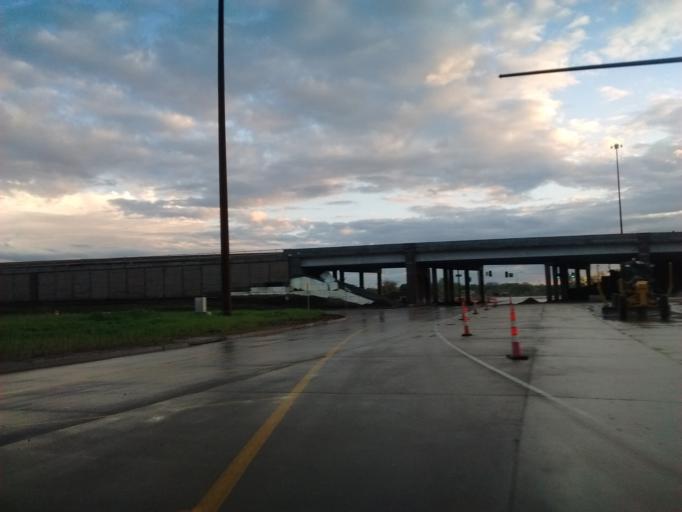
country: US
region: Iowa
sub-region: Woodbury County
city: Sioux City
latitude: 42.4875
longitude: -96.3942
